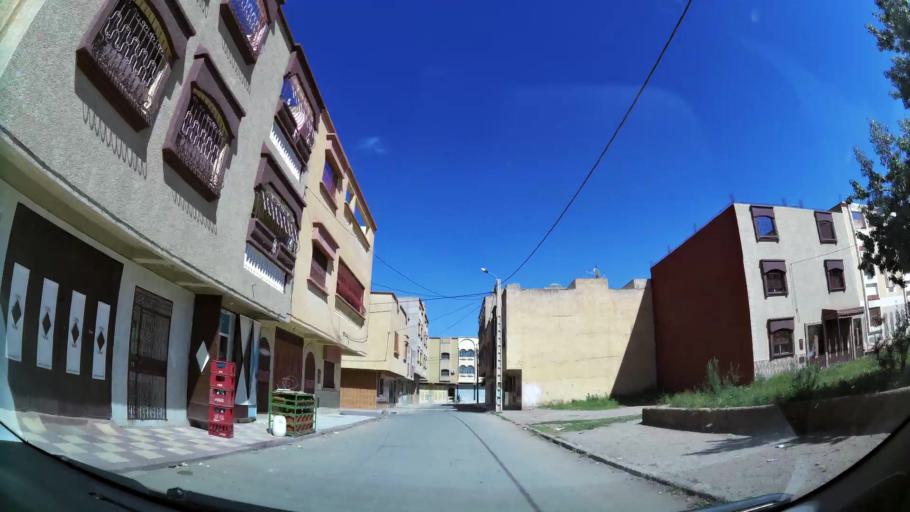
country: MA
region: Oriental
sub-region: Oujda-Angad
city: Oujda
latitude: 34.6835
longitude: -1.9438
